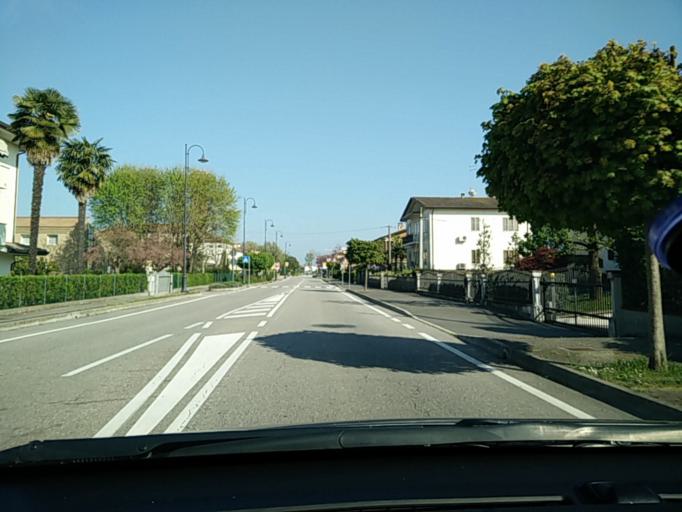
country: IT
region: Veneto
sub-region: Provincia di Venezia
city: Quarto d'Altino
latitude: 45.5603
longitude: 12.4326
